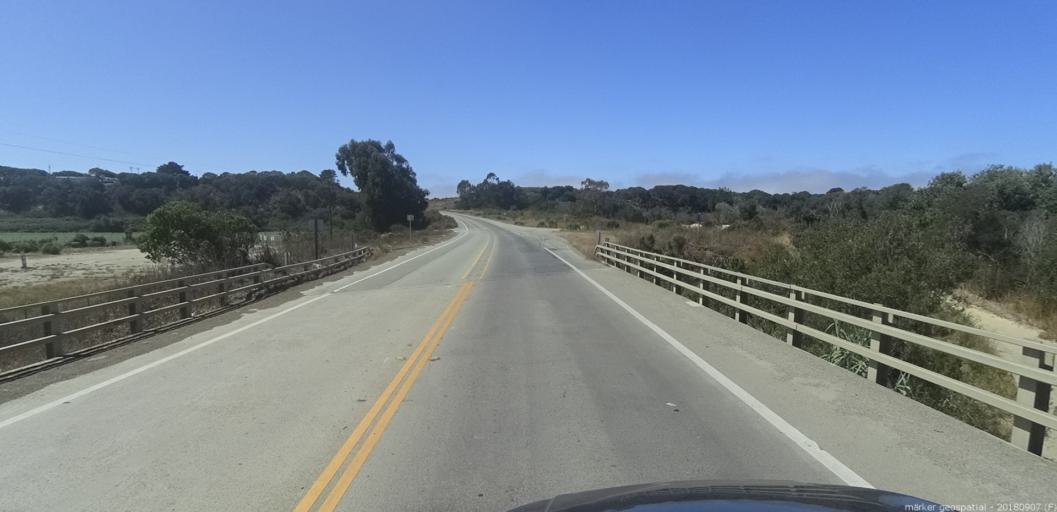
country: US
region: California
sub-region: Monterey County
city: Marina
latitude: 36.6777
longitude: -121.7464
